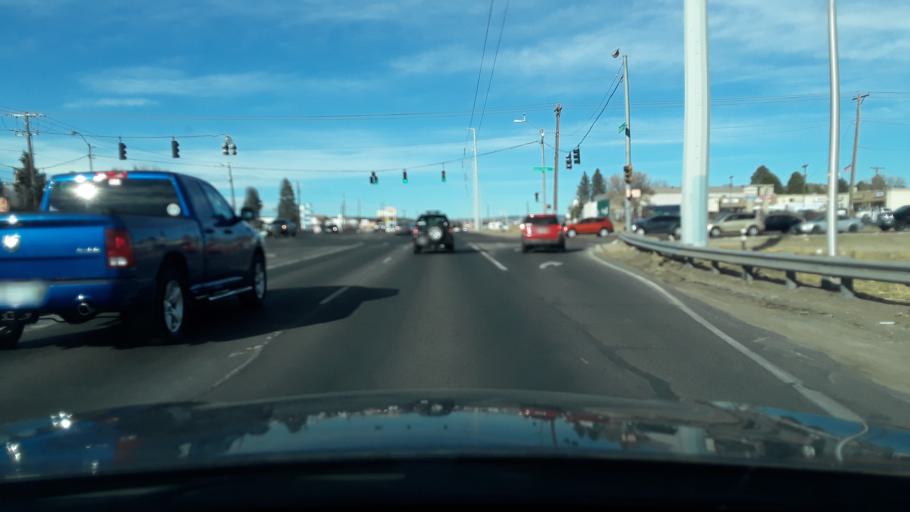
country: US
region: Colorado
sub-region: El Paso County
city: Colorado Springs
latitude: 38.8889
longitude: -104.8185
